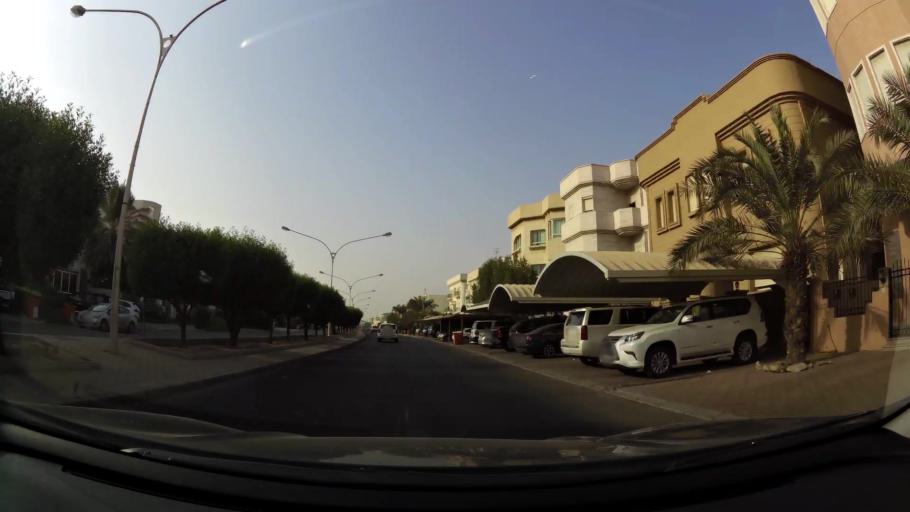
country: KW
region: Muhafazat Hawalli
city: Hawalli
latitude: 29.3100
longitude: 48.0083
